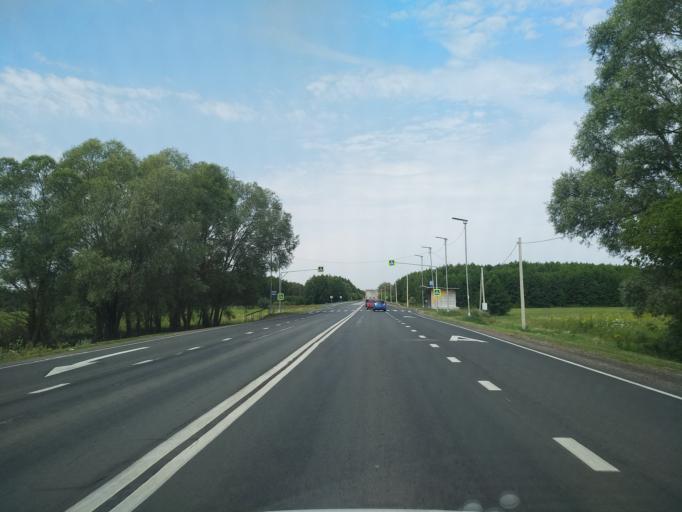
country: RU
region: Voronezj
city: Orlovo
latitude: 51.6807
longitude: 39.6009
